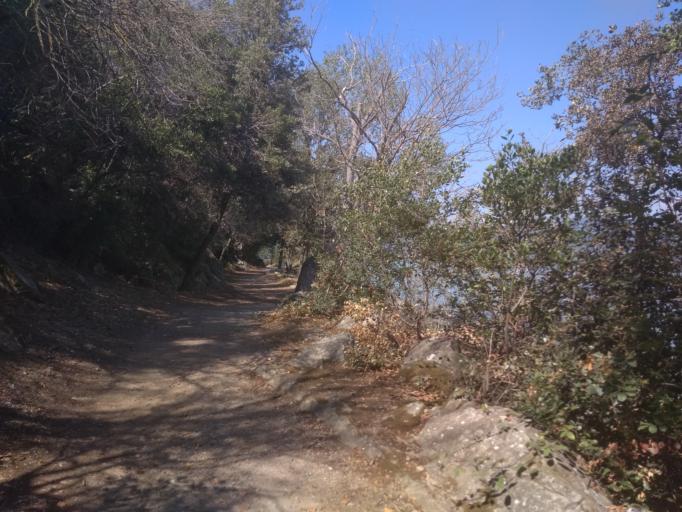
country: IT
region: Umbria
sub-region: Provincia di Perugia
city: Tuoro sul Trasimeno
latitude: 43.1772
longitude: 12.0939
